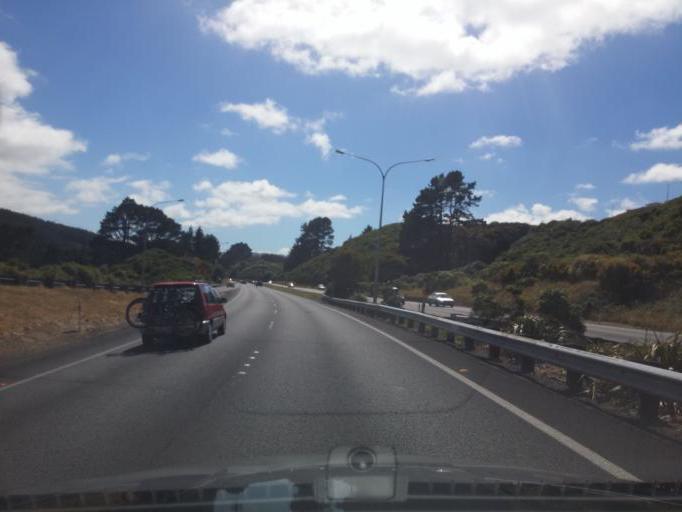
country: NZ
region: Wellington
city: Petone
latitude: -41.2036
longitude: 174.8218
